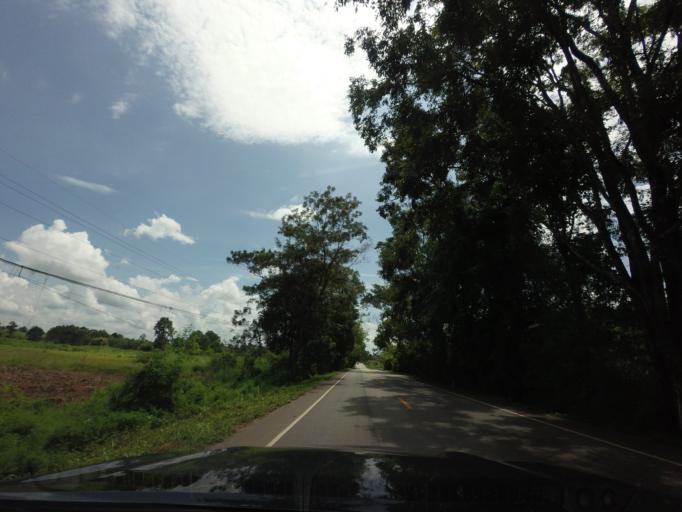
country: TH
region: Nong Khai
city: Pho Tak
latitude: 17.7997
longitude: 102.3486
